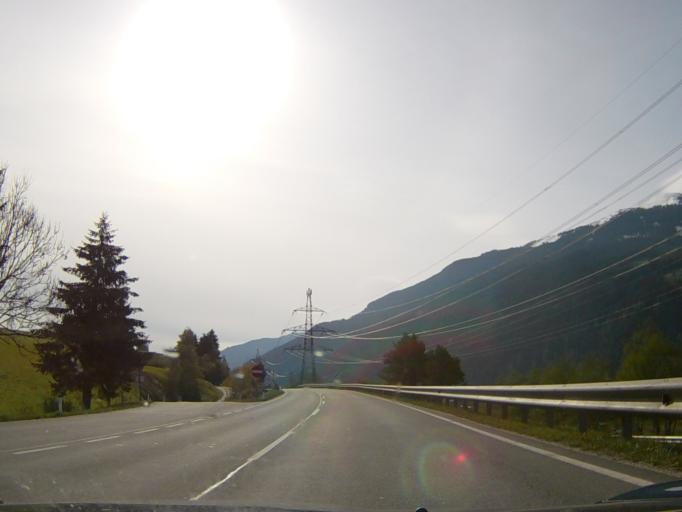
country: AT
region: Salzburg
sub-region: Politischer Bezirk Zell am See
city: Hollersbach im Pinzgau
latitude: 47.2818
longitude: 12.4050
